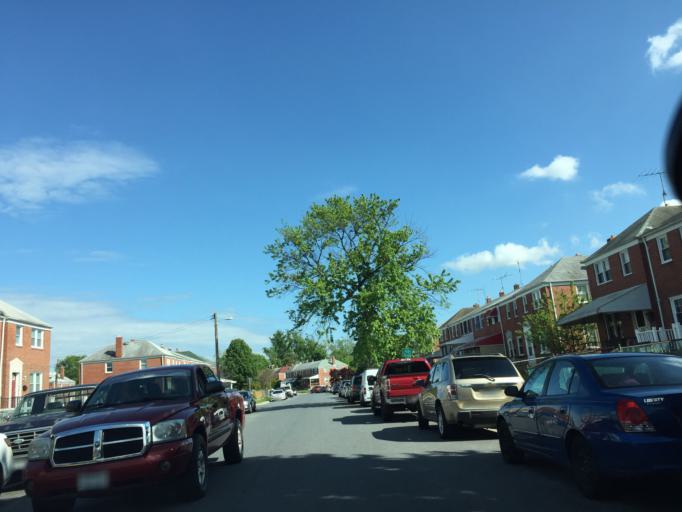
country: US
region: Maryland
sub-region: Baltimore County
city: Middle River
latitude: 39.3221
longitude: -76.4378
